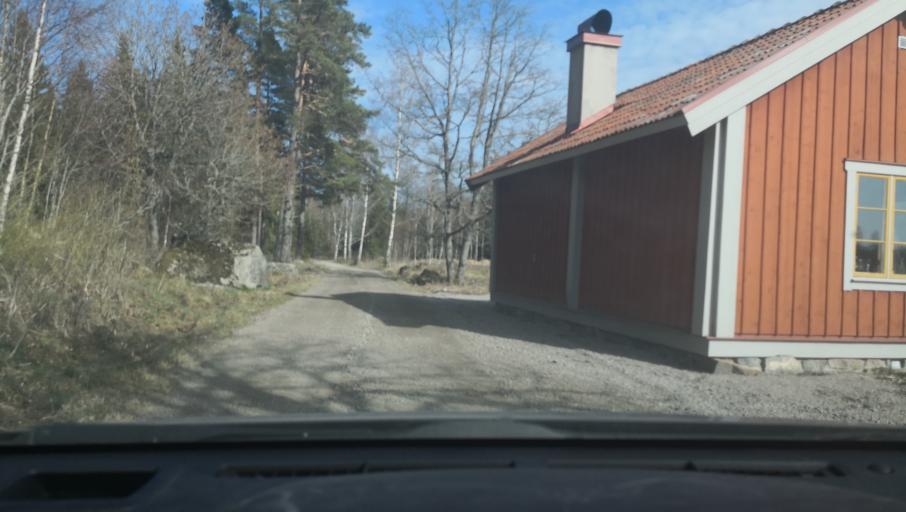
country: SE
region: Uppsala
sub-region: Heby Kommun
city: Heby
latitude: 59.8392
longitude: 16.8705
